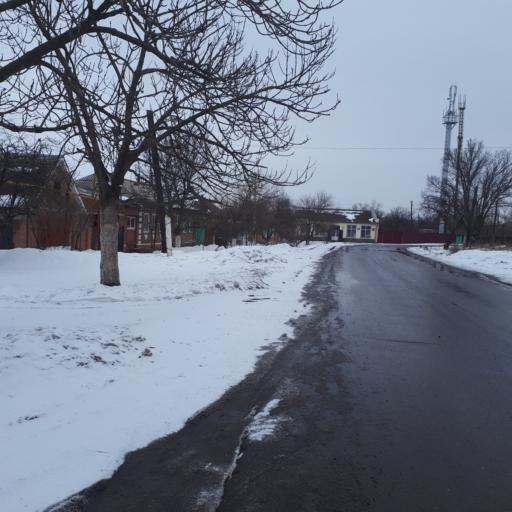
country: RU
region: Rostov
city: Krasnyy Sulin
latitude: 47.9027
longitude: 40.0440
